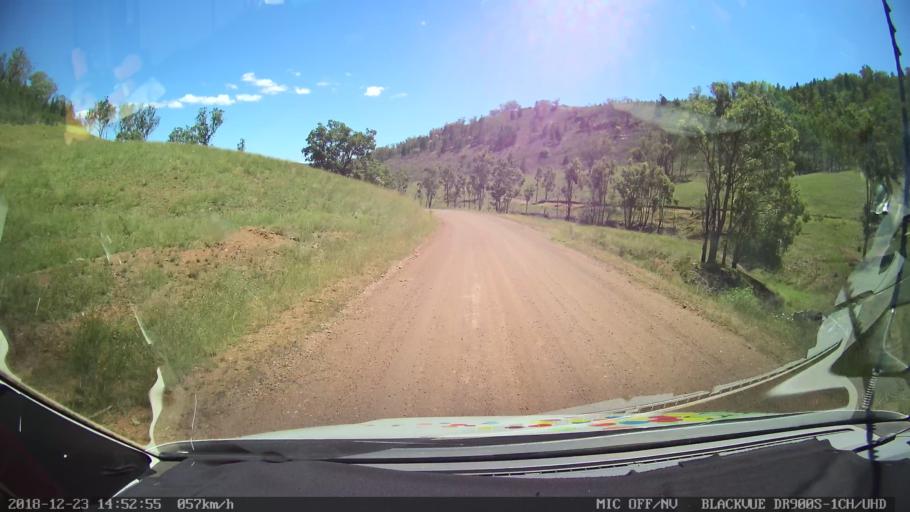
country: AU
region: New South Wales
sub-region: Tamworth Municipality
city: Manilla
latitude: -30.6875
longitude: 150.8526
